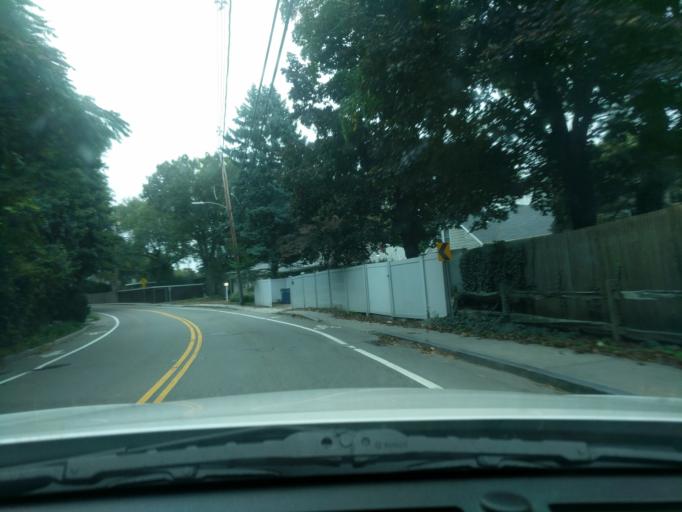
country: US
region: Massachusetts
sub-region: Middlesex County
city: Belmont
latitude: 42.3868
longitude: -71.1583
